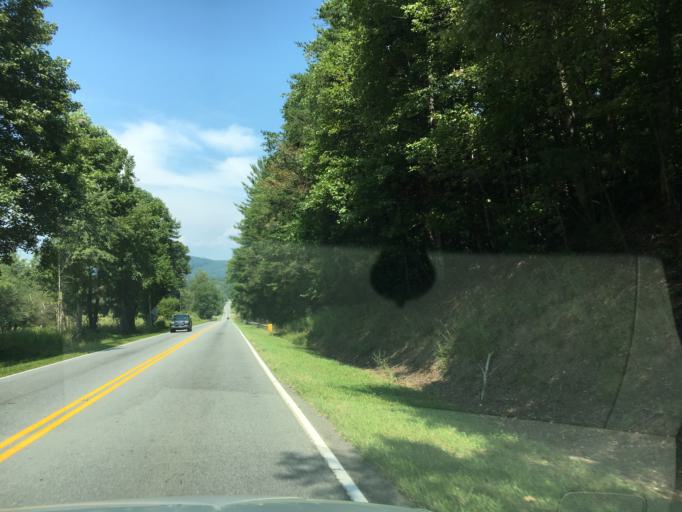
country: US
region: North Carolina
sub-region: McDowell County
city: West Marion
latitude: 35.6157
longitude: -81.9856
